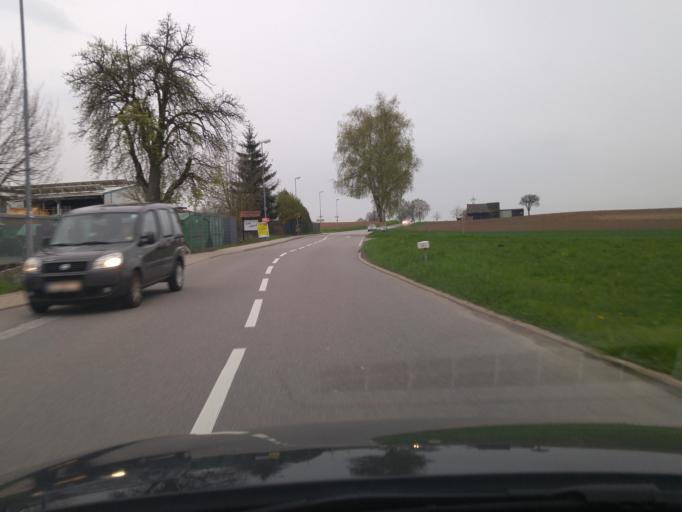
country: DE
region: Baden-Wuerttemberg
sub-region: Karlsruhe Region
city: Huffenhardt
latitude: 49.2885
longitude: 9.0841
